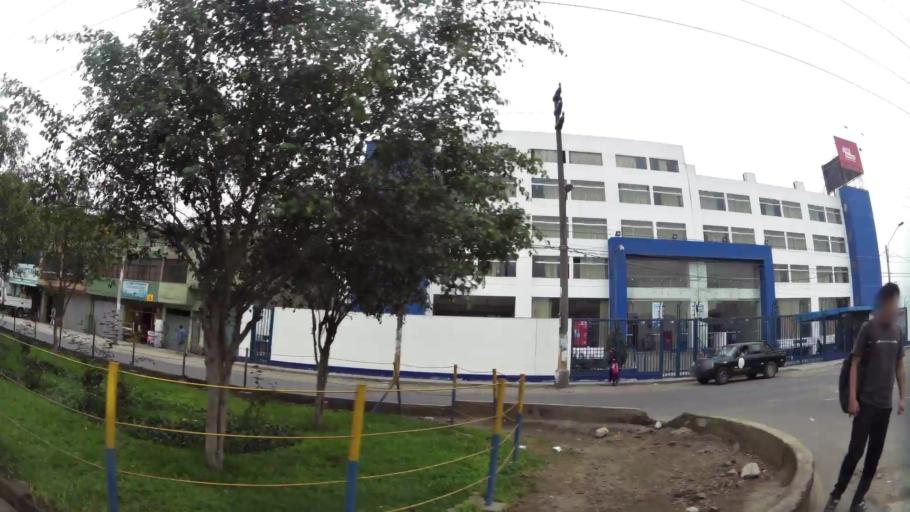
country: PE
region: Lima
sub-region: Lima
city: Independencia
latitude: -11.9835
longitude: -77.0100
